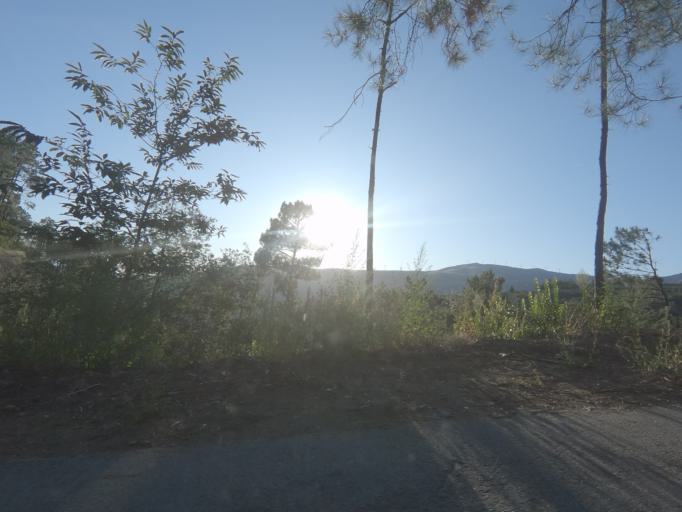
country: PT
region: Vila Real
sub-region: Peso da Regua
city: Godim
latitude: 41.1895
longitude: -7.8295
